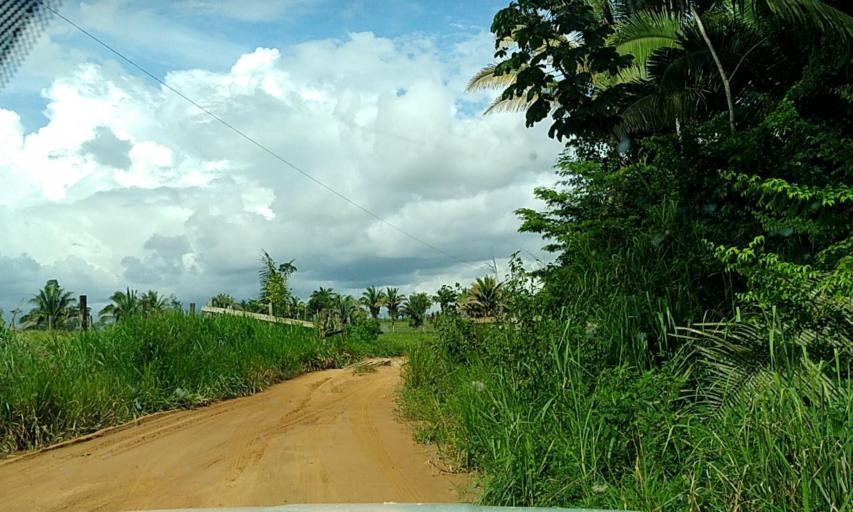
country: BR
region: Para
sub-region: Altamira
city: Altamira
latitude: -3.2319
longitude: -52.7307
